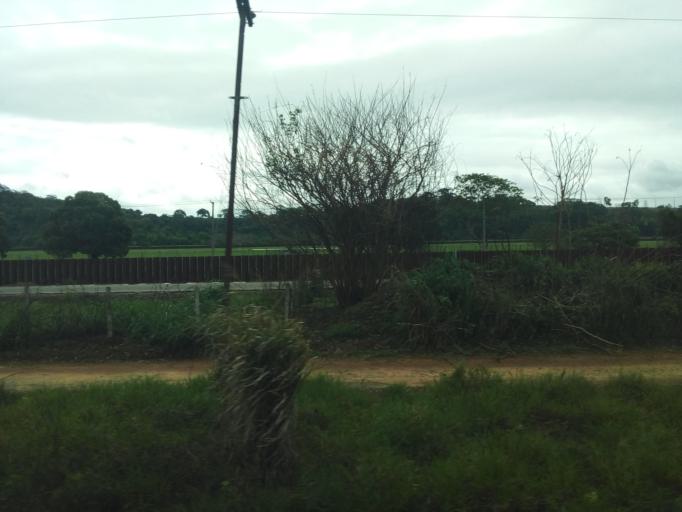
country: BR
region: Minas Gerais
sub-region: Ipatinga
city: Ipatinga
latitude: -19.4781
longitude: -42.4883
